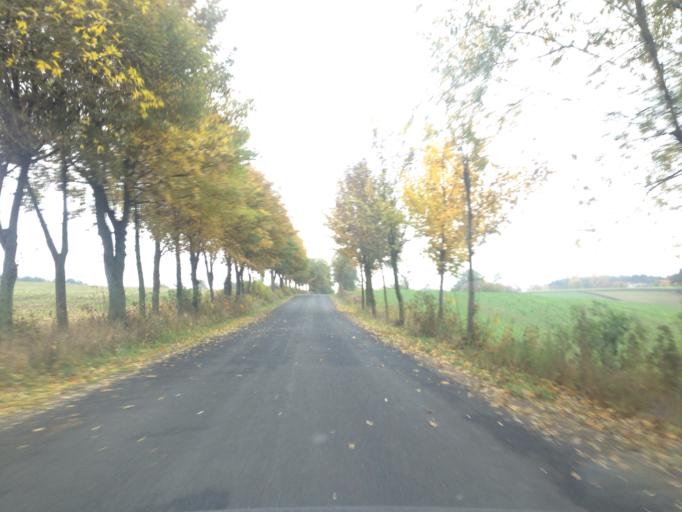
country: PL
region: Kujawsko-Pomorskie
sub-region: Powiat brodnicki
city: Brzozie
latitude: 53.2948
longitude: 19.6967
